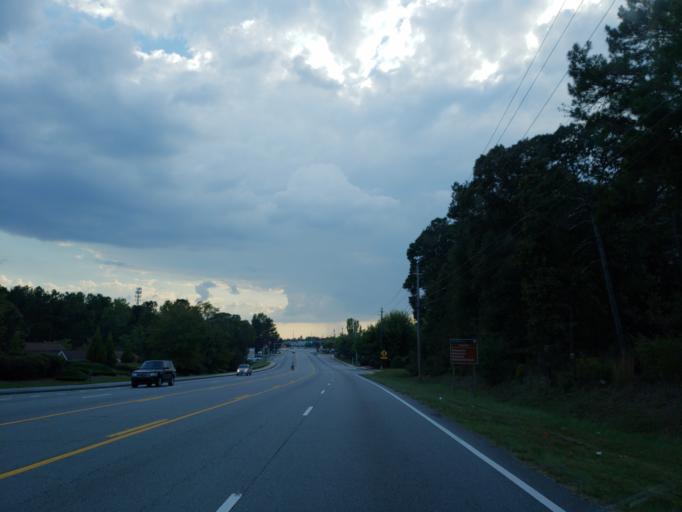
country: US
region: Georgia
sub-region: Cobb County
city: Fair Oaks
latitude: 33.9093
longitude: -84.5997
